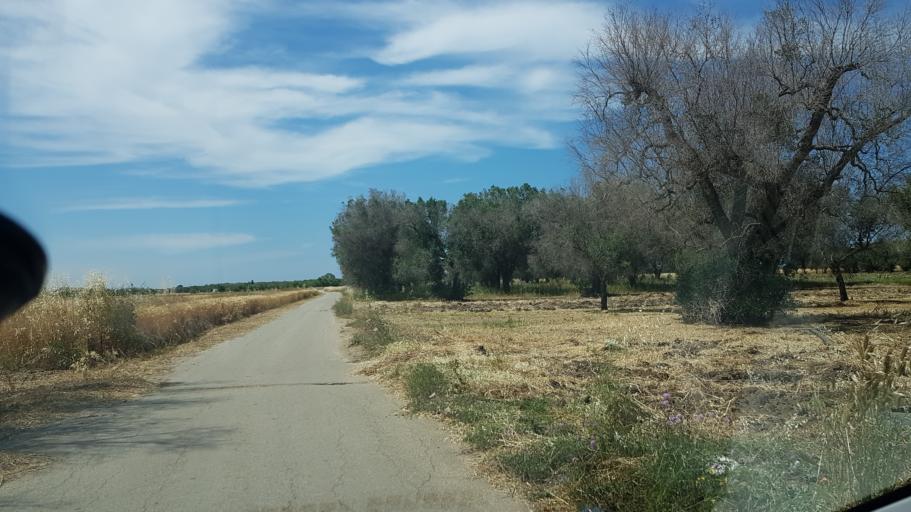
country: IT
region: Apulia
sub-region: Provincia di Brindisi
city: San Pietro Vernotico
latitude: 40.5313
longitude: 17.9999
